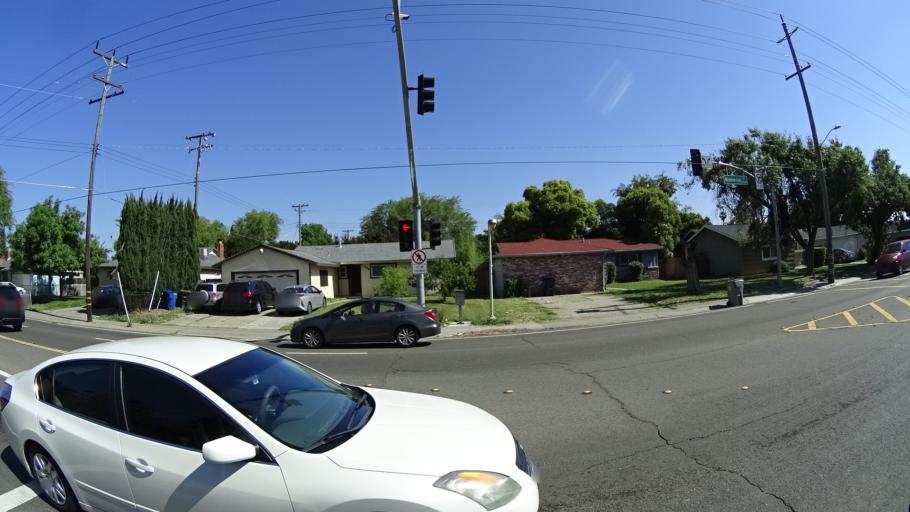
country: US
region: California
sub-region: Sacramento County
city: Parkway
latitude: 38.4813
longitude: -121.4917
